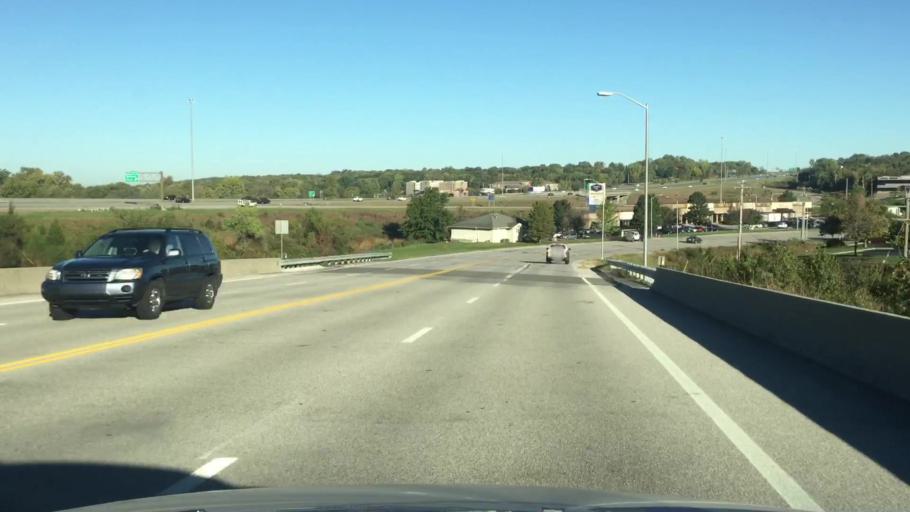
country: US
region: Kansas
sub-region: Johnson County
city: Lenexa
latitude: 38.9959
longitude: -94.7790
